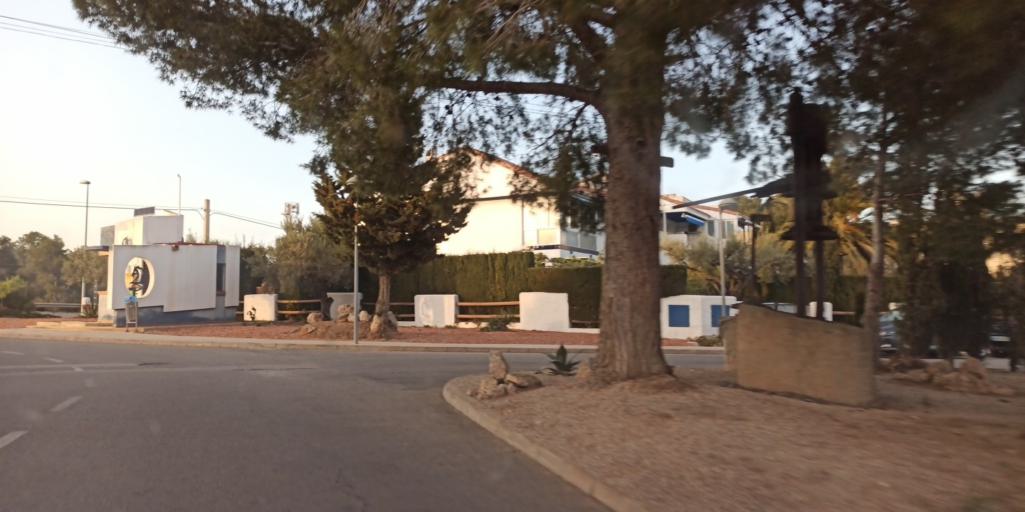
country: ES
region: Catalonia
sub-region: Provincia de Tarragona
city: L'Ampolla
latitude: 40.8240
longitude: 0.7294
